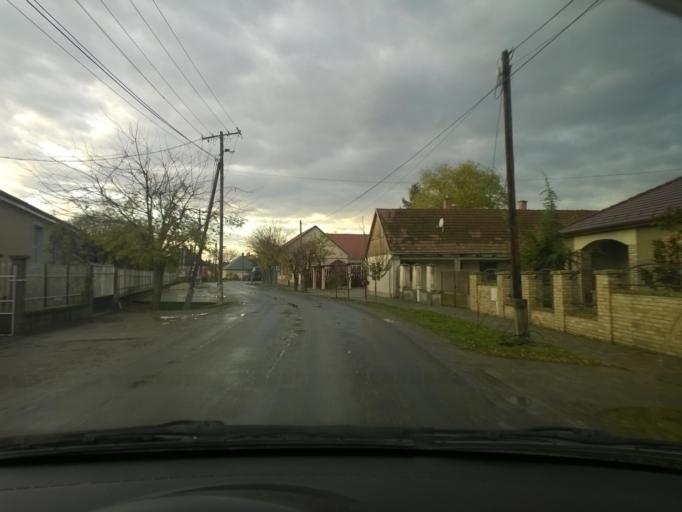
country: HU
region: Bacs-Kiskun
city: Kalocsa
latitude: 46.4902
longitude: 19.0696
